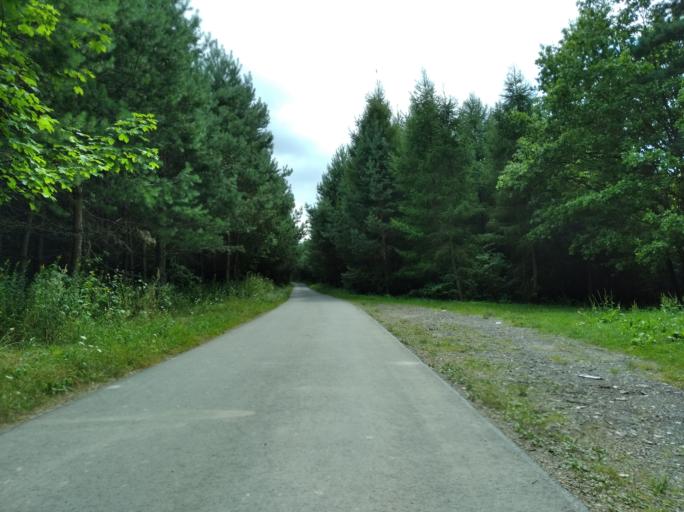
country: PL
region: Subcarpathian Voivodeship
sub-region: Powiat krosnienski
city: Odrzykon
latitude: 49.7814
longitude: 21.7204
